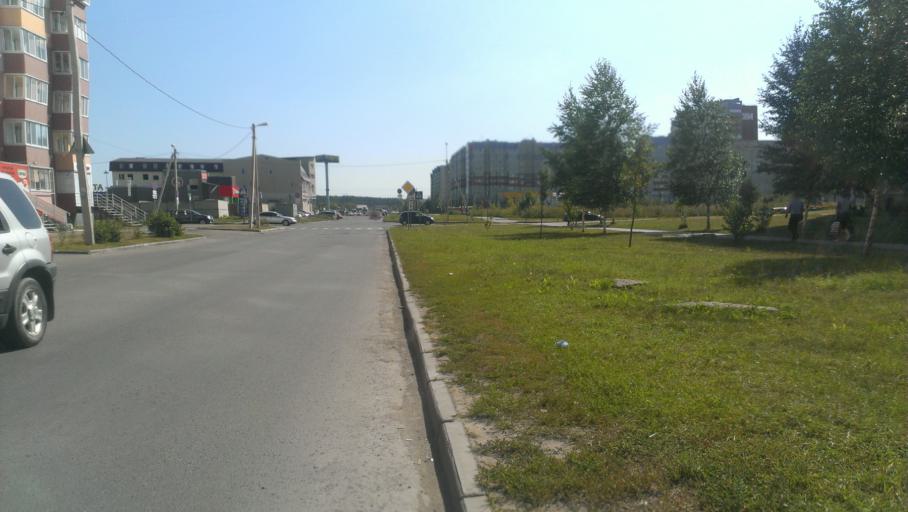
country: RU
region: Altai Krai
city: Novosilikatnyy
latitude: 53.3307
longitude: 83.6844
